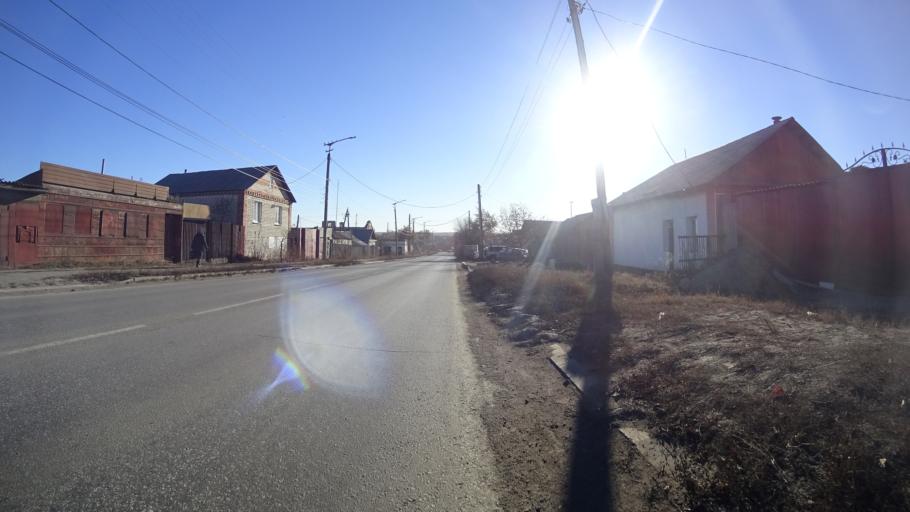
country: RU
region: Chelyabinsk
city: Troitsk
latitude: 54.0989
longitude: 61.5627
